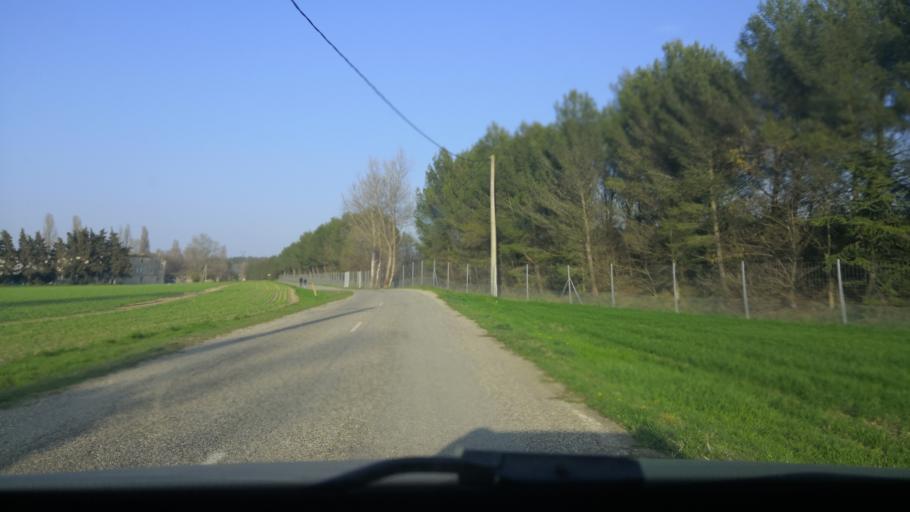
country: FR
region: Rhone-Alpes
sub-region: Departement de la Drome
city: Montboucher-sur-Jabron
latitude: 44.5508
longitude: 4.8271
